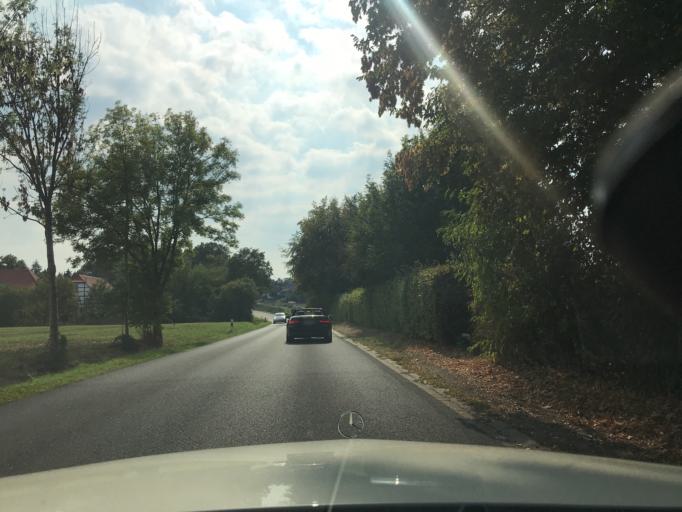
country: DE
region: North Rhine-Westphalia
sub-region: Regierungsbezirk Arnsberg
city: Werl
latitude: 51.5808
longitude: 7.8679
